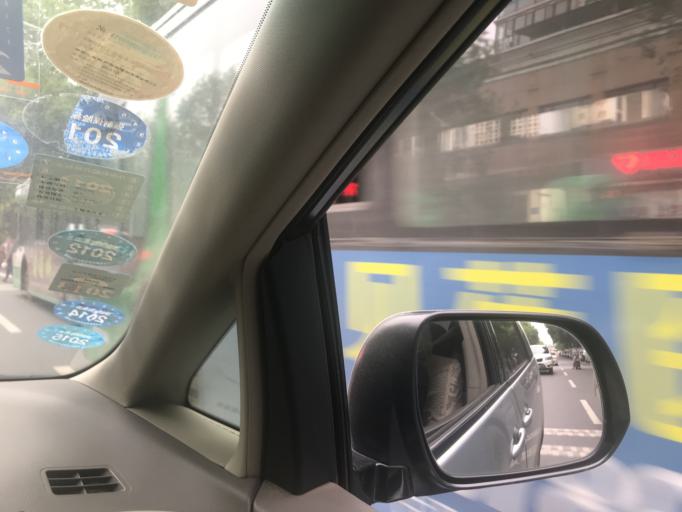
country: CN
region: Hubei
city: Wuhan
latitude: 30.5522
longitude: 114.2652
